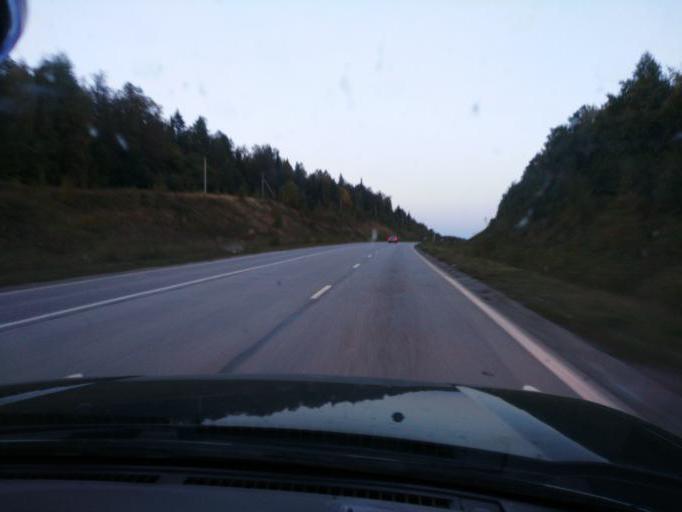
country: RU
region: Perm
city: Verkhnechusovskiye Gorodki
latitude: 58.2782
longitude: 56.9297
